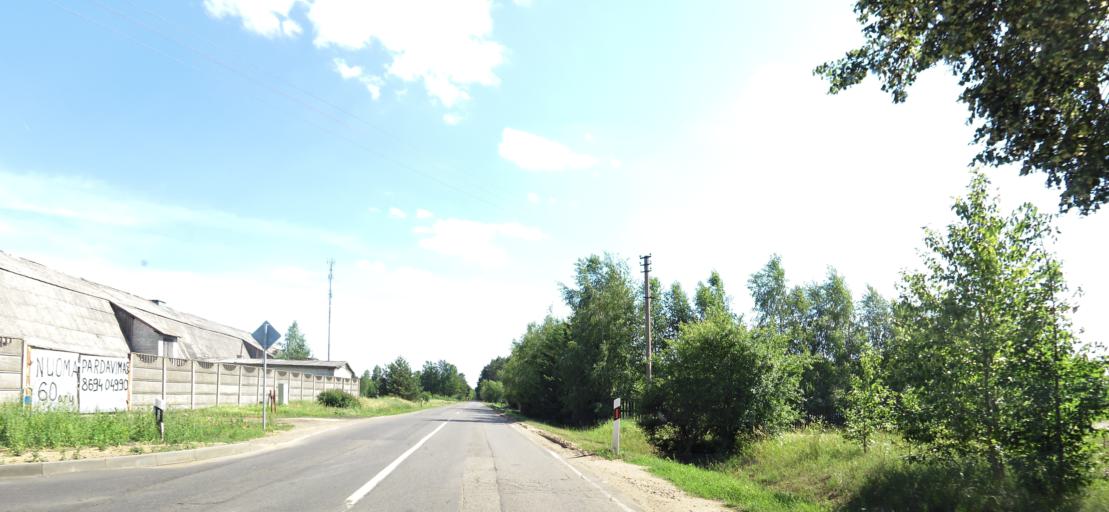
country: LT
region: Vilnius County
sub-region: Vilnius
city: Fabijoniskes
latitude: 54.8002
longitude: 25.3484
